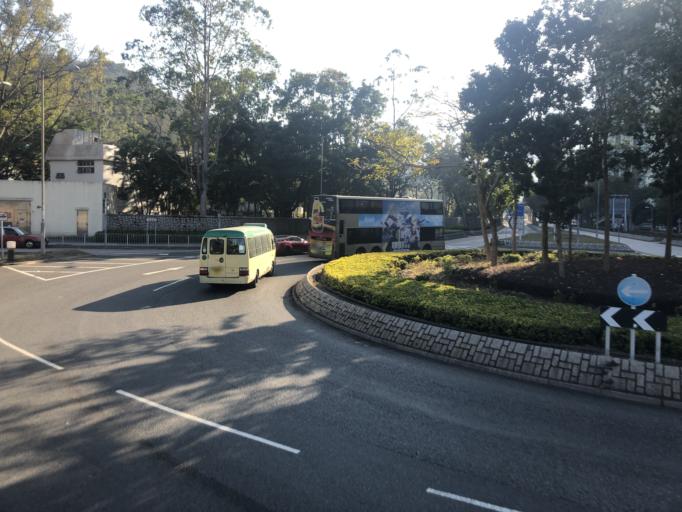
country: HK
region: Sai Kung
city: Sai Kung
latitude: 22.3167
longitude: 114.2705
